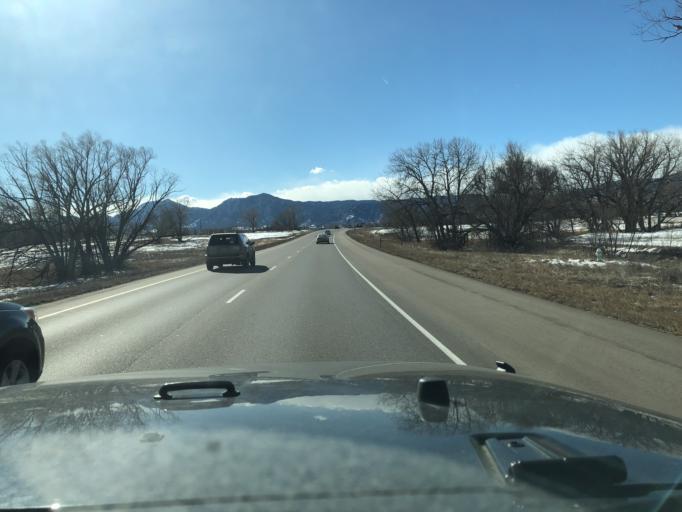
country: US
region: Colorado
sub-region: Boulder County
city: Boulder
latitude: 40.0549
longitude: -105.2291
